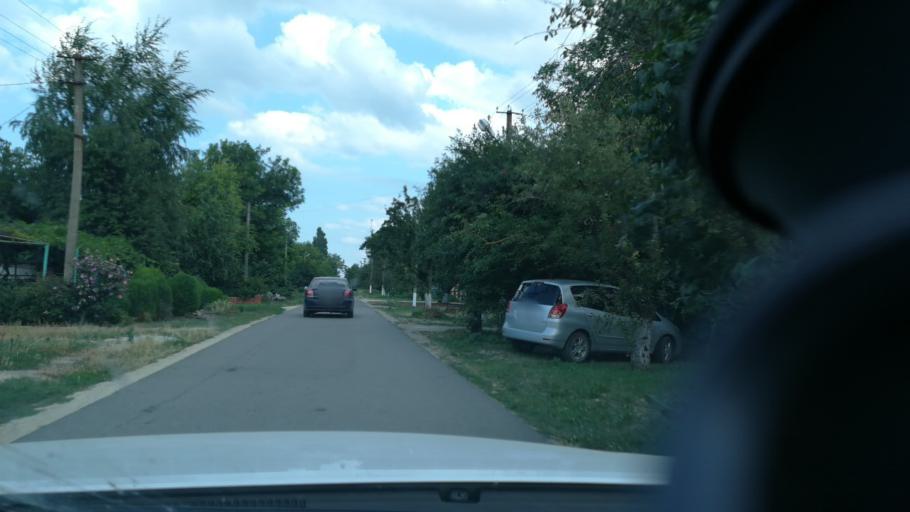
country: RU
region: Krasnodarskiy
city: Yurovka
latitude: 45.1172
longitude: 37.4168
